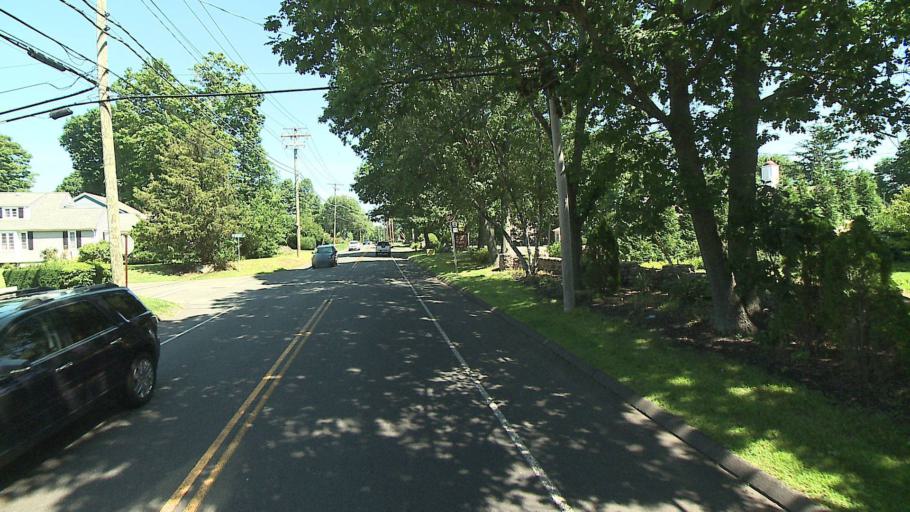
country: US
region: Connecticut
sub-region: Fairfield County
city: Trumbull
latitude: 41.2439
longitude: -73.2217
